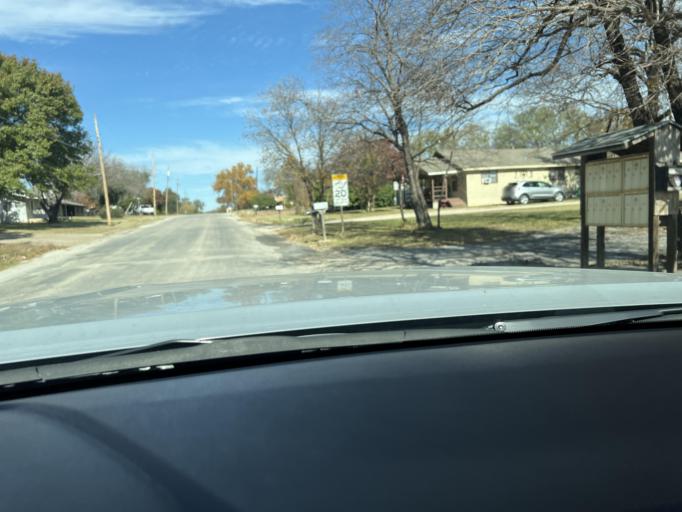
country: US
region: Texas
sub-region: Eastland County
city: Eastland
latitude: 32.3960
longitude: -98.8307
